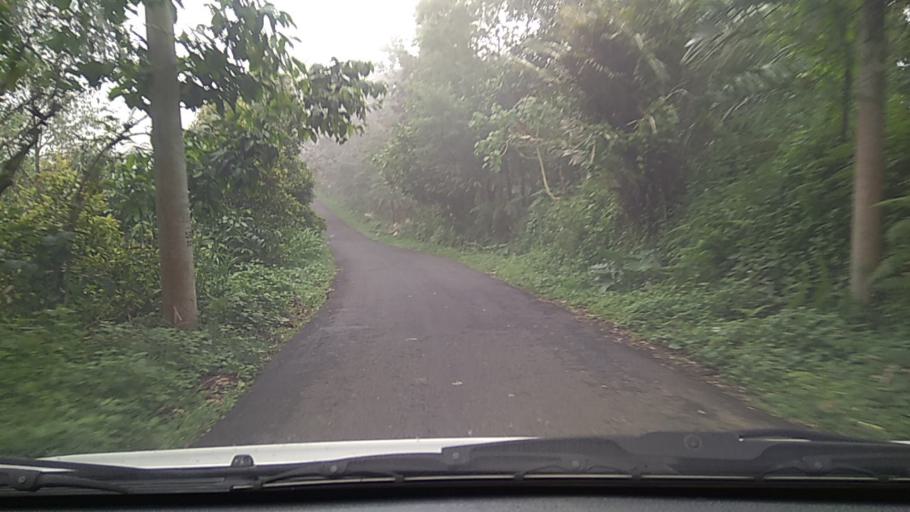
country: ID
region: Bali
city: Banjar Ambengan
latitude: -8.2017
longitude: 115.1758
